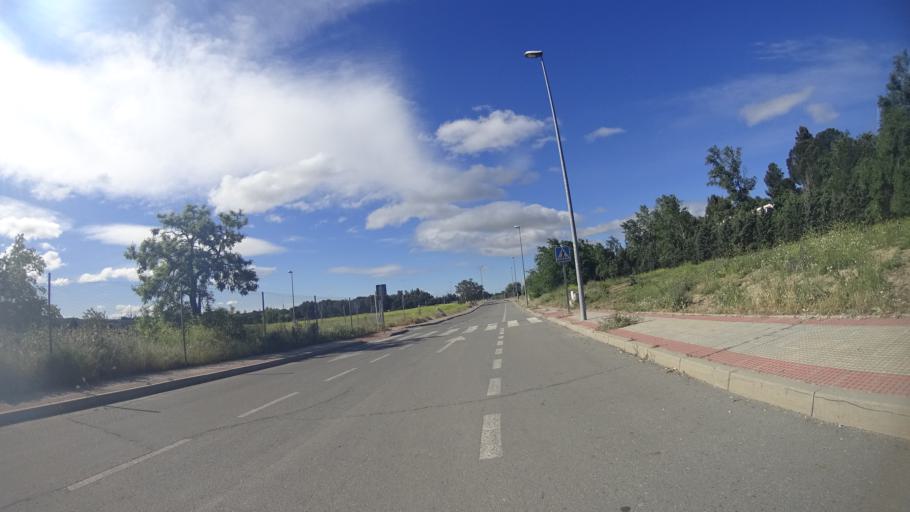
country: ES
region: Madrid
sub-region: Provincia de Madrid
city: Villanueva del Pardillo
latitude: 40.4926
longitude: -3.9405
